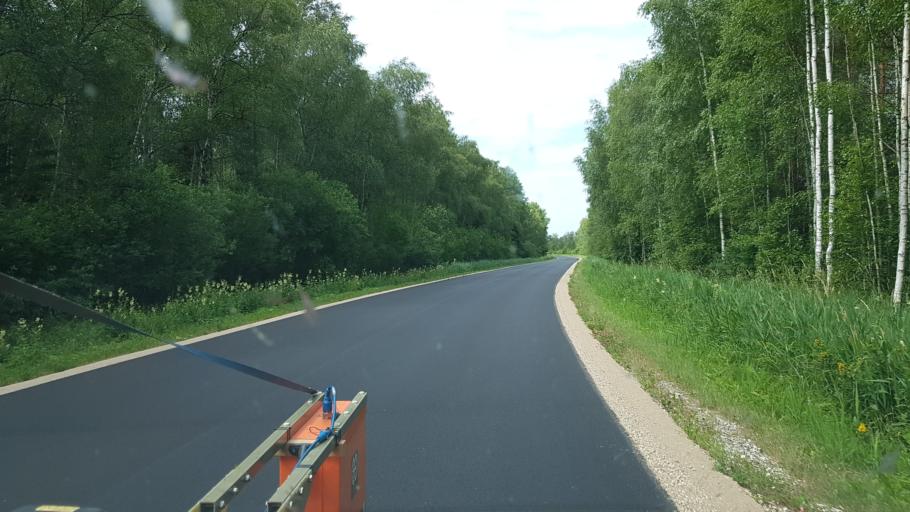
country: EE
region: Paernumaa
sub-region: Audru vald
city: Audru
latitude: 58.6216
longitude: 24.2431
